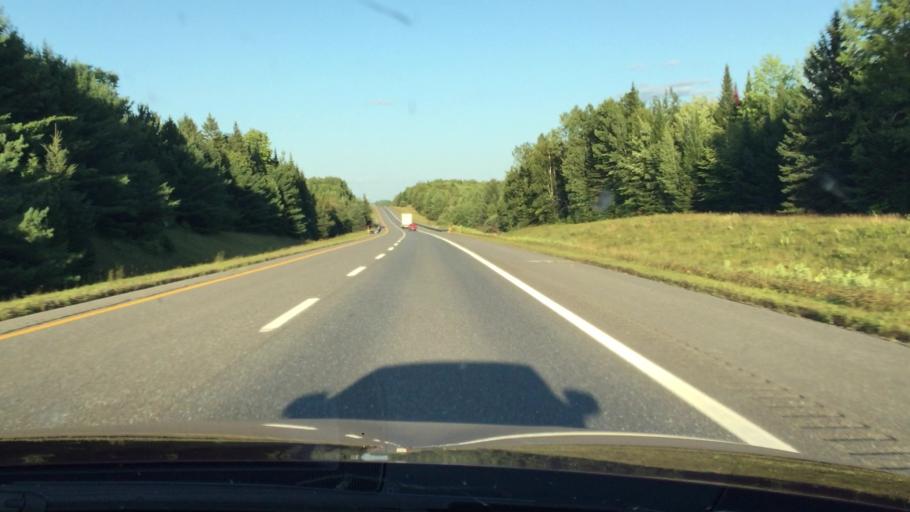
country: US
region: Maine
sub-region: Aroostook County
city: Hodgdon
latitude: 46.1399
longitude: -68.0152
